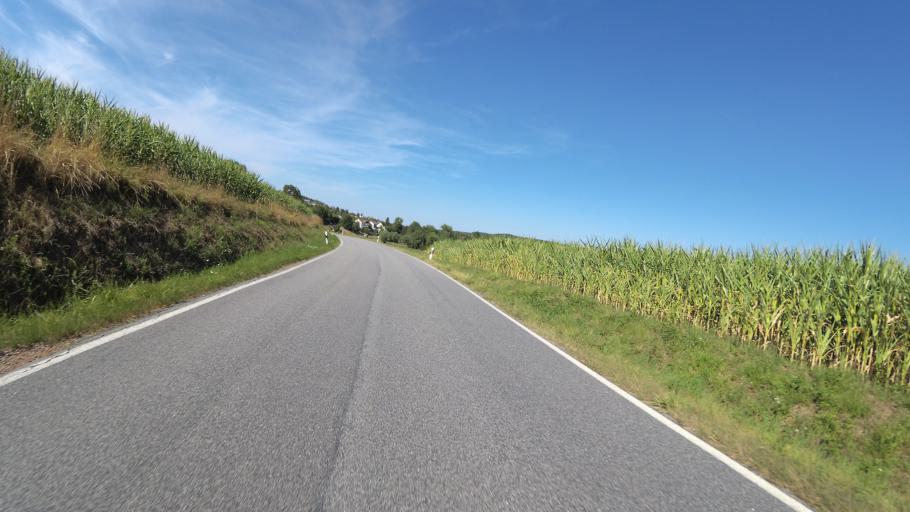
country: DE
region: Rheinland-Pfalz
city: Hornbach
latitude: 49.1632
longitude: 7.3086
